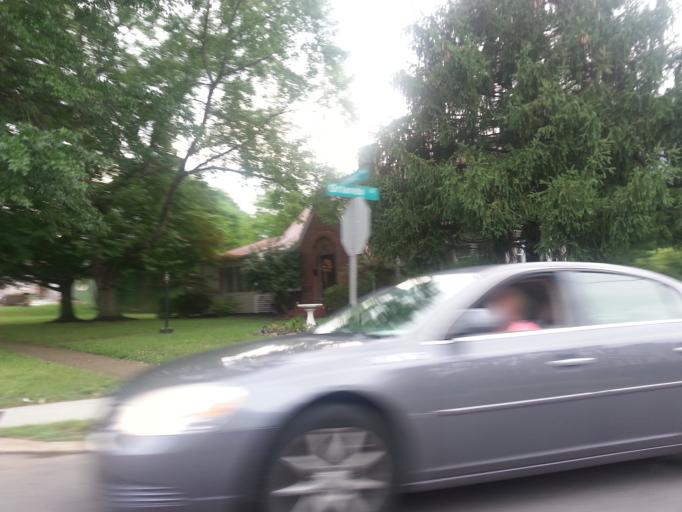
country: US
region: Tennessee
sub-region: Knox County
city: Knoxville
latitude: 36.0080
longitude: -83.9185
